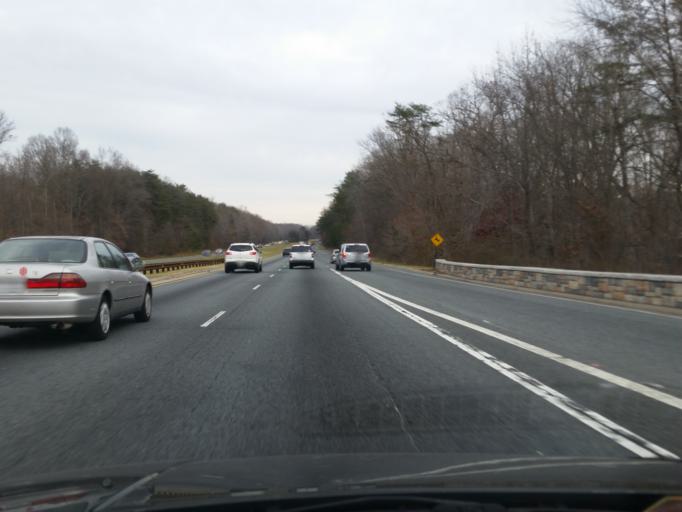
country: US
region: Maryland
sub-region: Prince George's County
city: South Laurel
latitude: 39.0360
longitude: -76.8506
